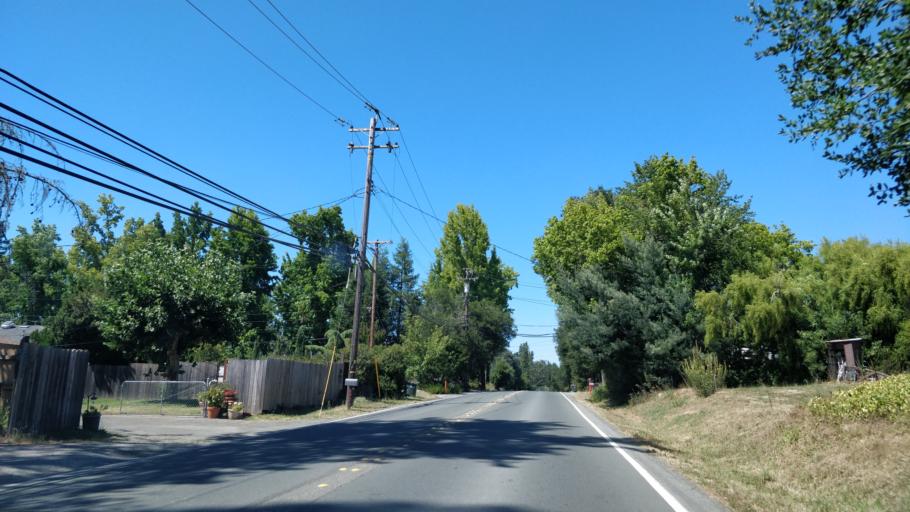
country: US
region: California
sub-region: Sonoma County
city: Forestville
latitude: 38.4841
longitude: -122.8948
